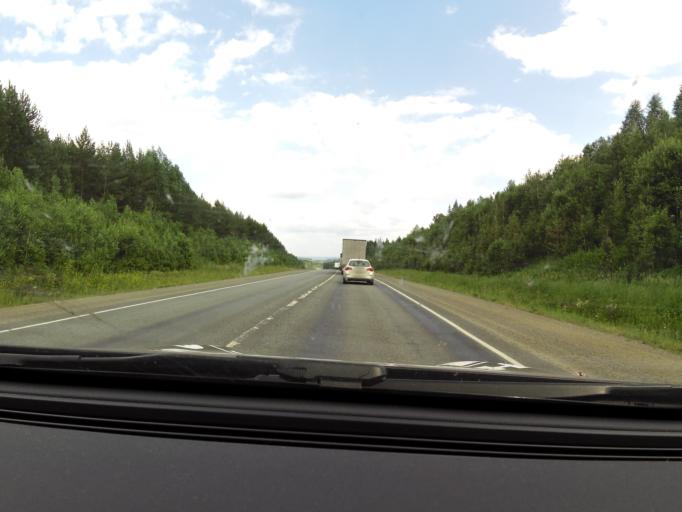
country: RU
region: Sverdlovsk
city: Bisert'
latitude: 56.8271
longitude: 58.9991
